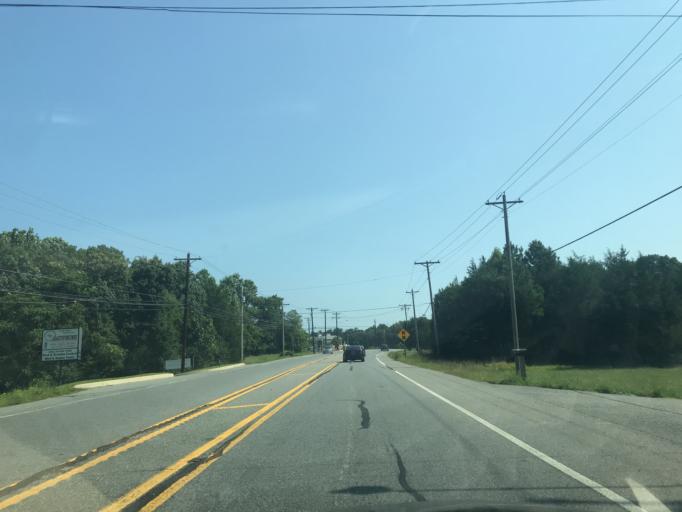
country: US
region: Maryland
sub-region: Calvert County
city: Prince Frederick
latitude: 38.5314
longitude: -76.6112
